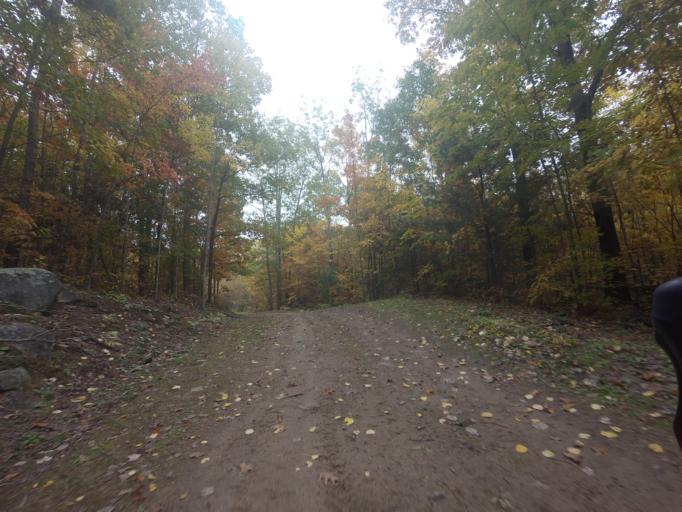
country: CA
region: Ontario
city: Petawawa
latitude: 45.7520
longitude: -77.3548
